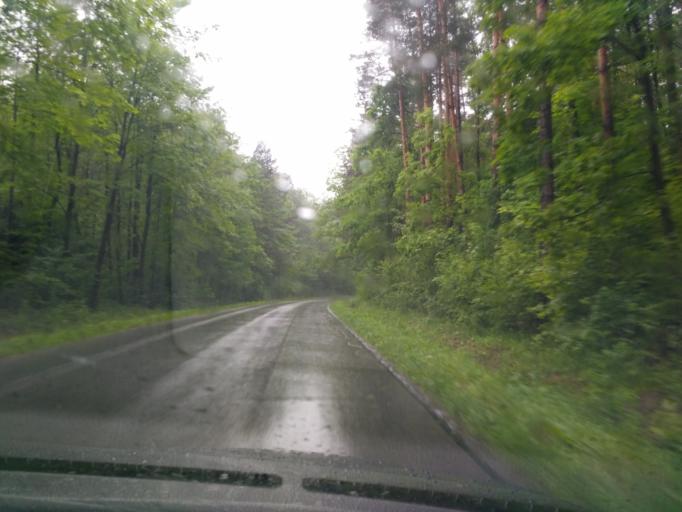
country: PL
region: Subcarpathian Voivodeship
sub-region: Powiat jasielski
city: Debowiec
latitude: 49.6609
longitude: 21.4321
